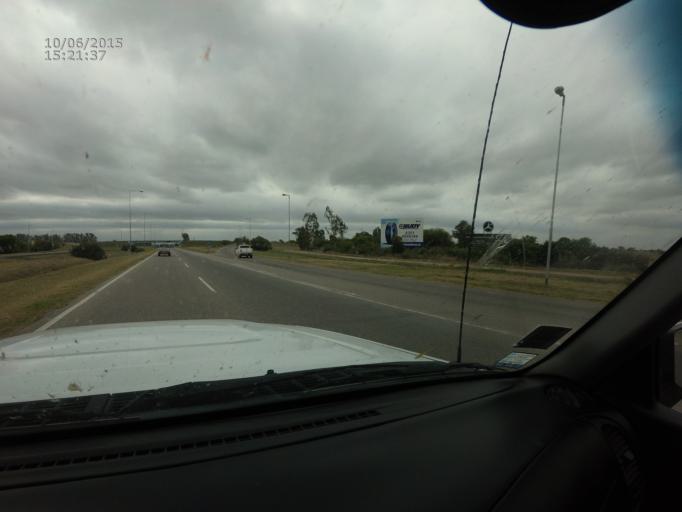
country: AR
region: Cordoba
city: Toledo
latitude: -31.4877
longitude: -64.0258
